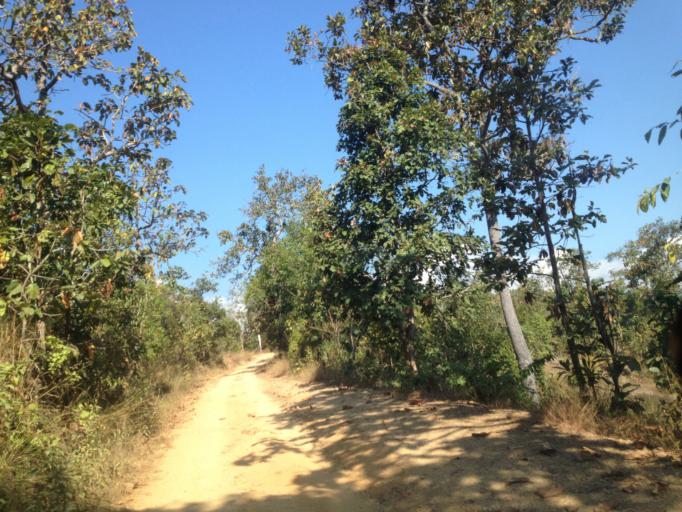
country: TH
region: Mae Hong Son
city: Ban Huai I Huak
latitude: 18.1175
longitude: 98.2077
